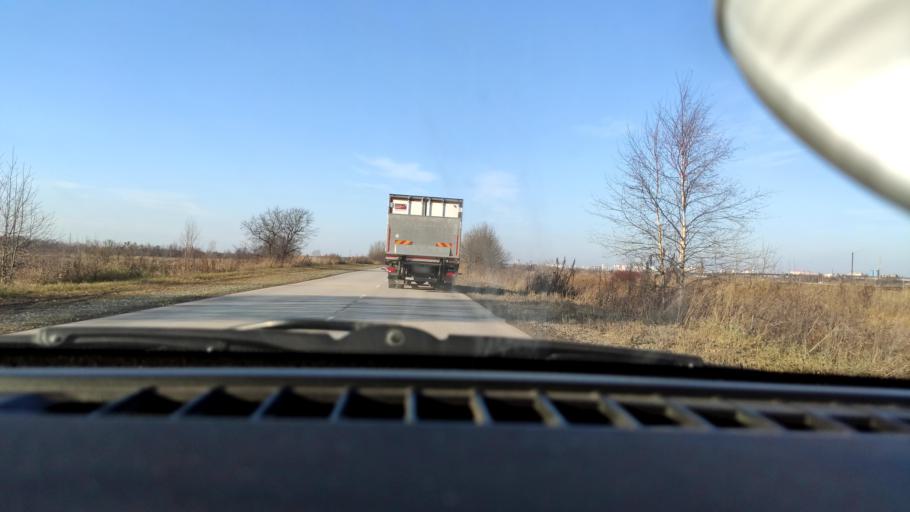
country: RU
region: Perm
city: Kondratovo
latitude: 58.0000
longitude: 56.0729
